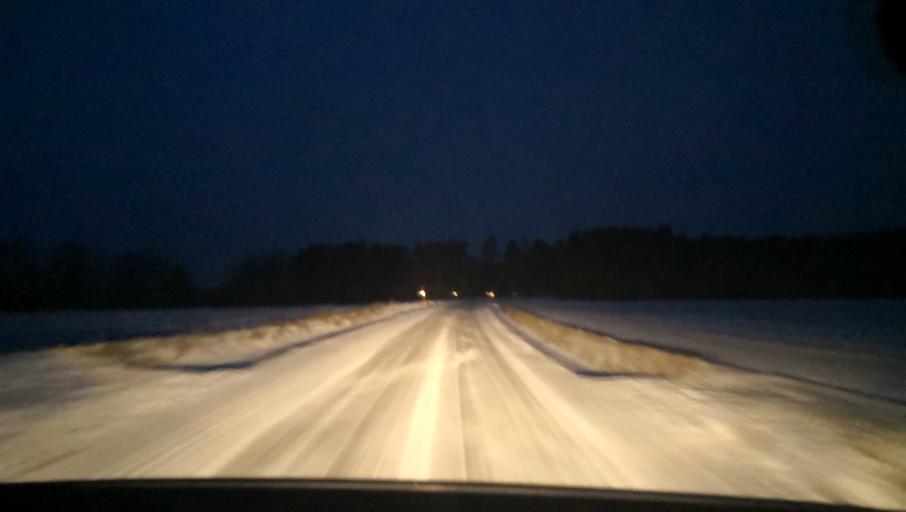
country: SE
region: Uppsala
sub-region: Heby Kommun
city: Tarnsjo
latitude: 60.2637
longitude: 16.7926
